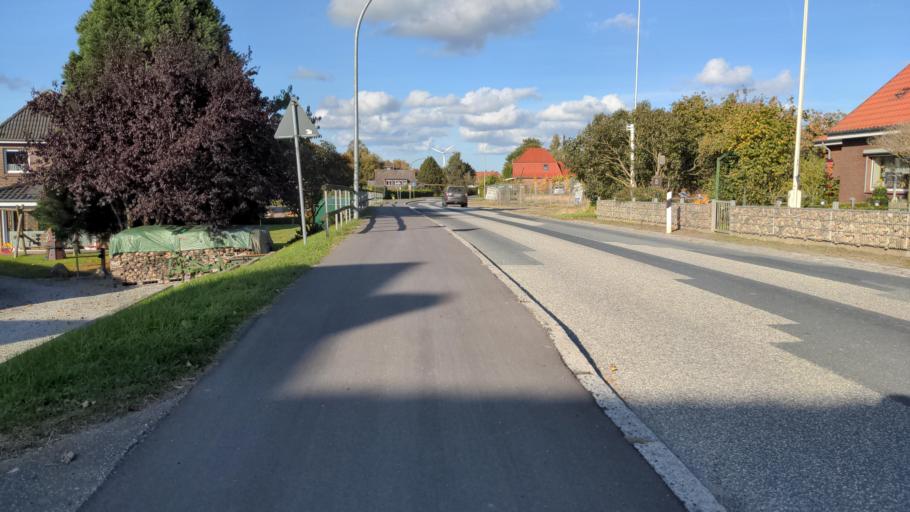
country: DE
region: Schleswig-Holstein
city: Beschendorf
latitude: 54.1800
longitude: 10.8777
